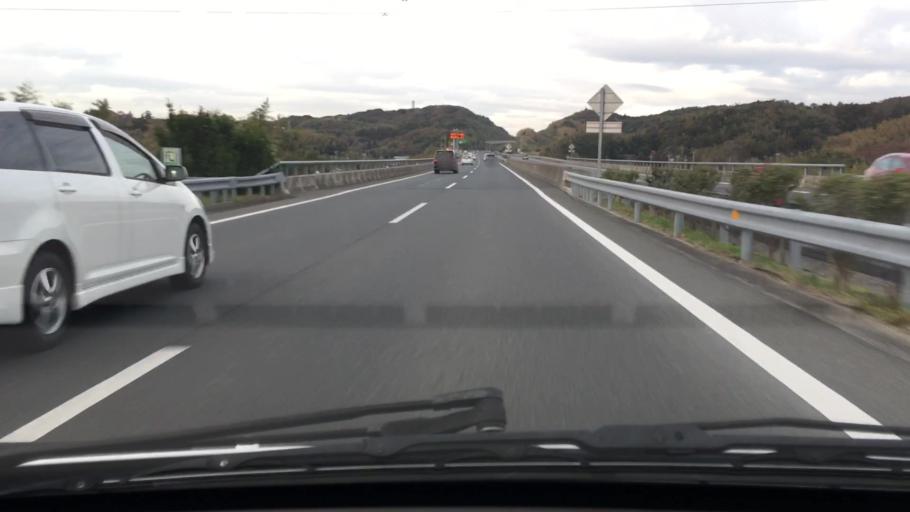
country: JP
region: Chiba
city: Kimitsu
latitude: 35.3113
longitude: 139.9428
